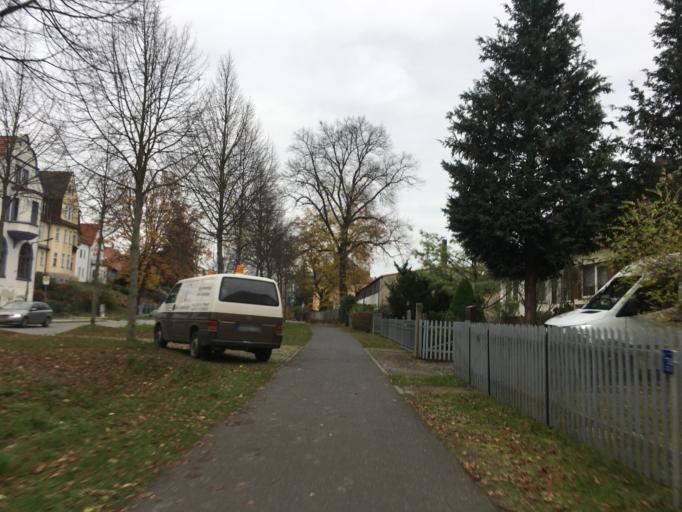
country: DE
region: Brandenburg
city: Frankfurt (Oder)
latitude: 52.3285
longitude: 14.5545
